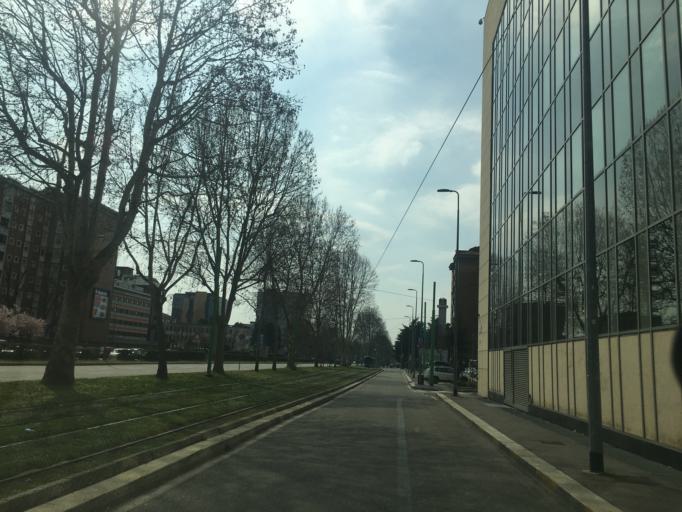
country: IT
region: Lombardy
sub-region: Citta metropolitana di Milano
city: Sesto San Giovanni
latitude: 45.5284
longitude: 9.2128
